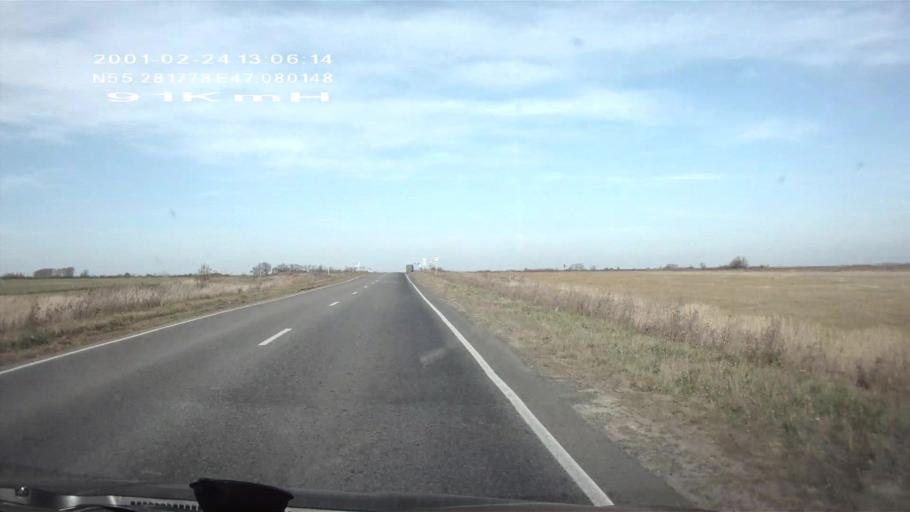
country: RU
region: Chuvashia
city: Ibresi
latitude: 55.2817
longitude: 47.0802
